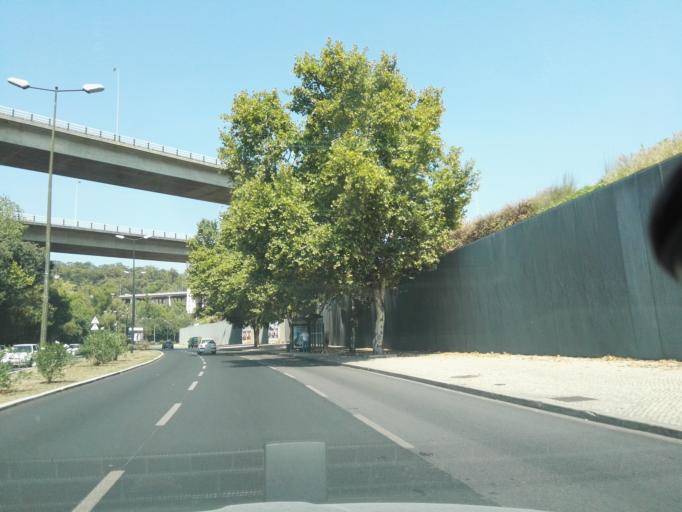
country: PT
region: Lisbon
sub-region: Lisbon
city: Lisbon
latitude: 38.7189
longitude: -9.1747
